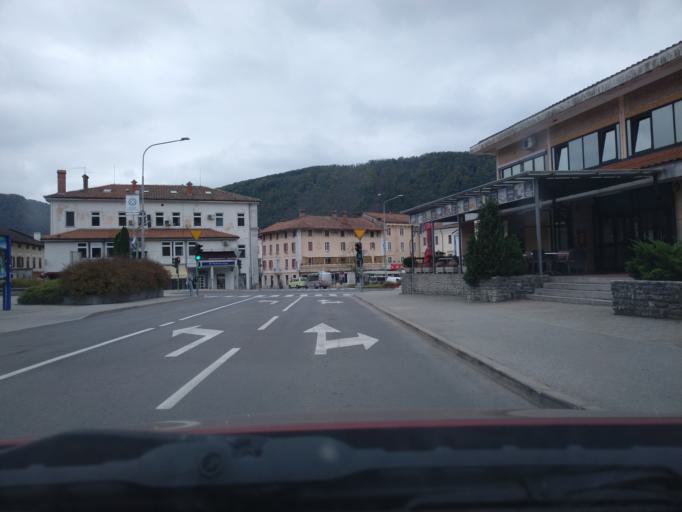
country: SI
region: Tolmin
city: Tolmin
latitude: 46.1832
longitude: 13.7329
